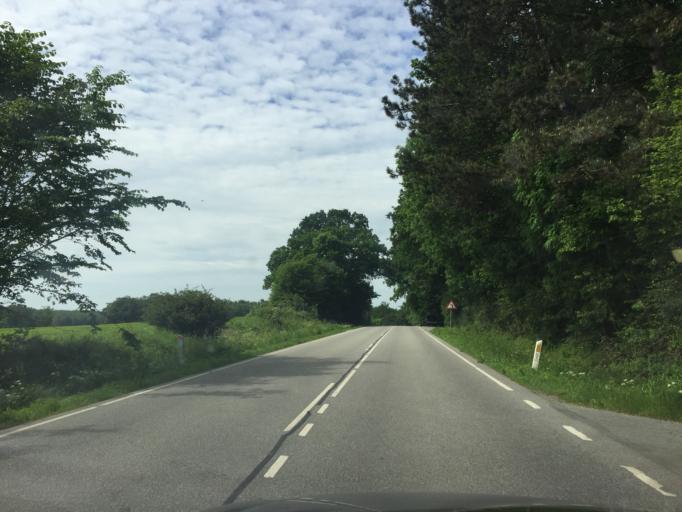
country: DK
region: South Denmark
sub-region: Nyborg Kommune
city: Ullerslev
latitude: 55.2412
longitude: 10.6542
